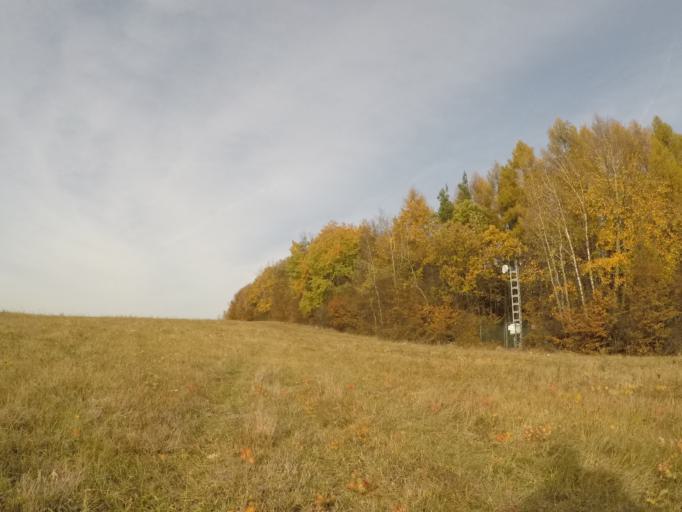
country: SK
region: Presovsky
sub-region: Okres Presov
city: Presov
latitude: 48.9221
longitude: 21.2234
